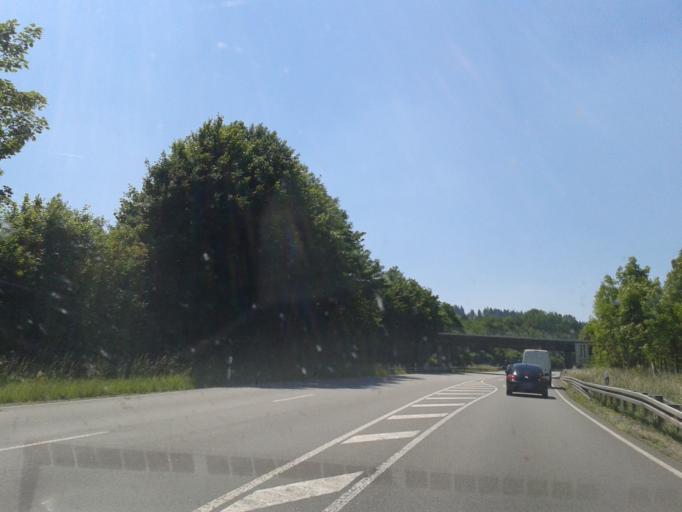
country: DE
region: North Rhine-Westphalia
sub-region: Regierungsbezirk Detmold
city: Horn
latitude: 51.8625
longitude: 8.9538
